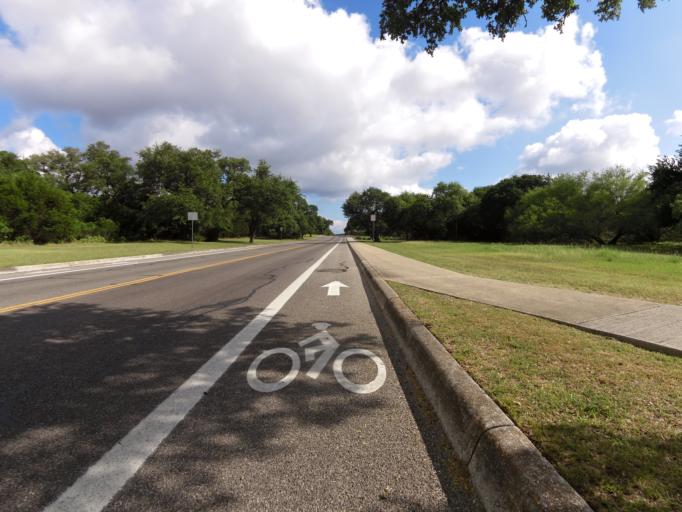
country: US
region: Texas
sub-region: Bexar County
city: Shavano Park
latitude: 29.5857
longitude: -98.6070
